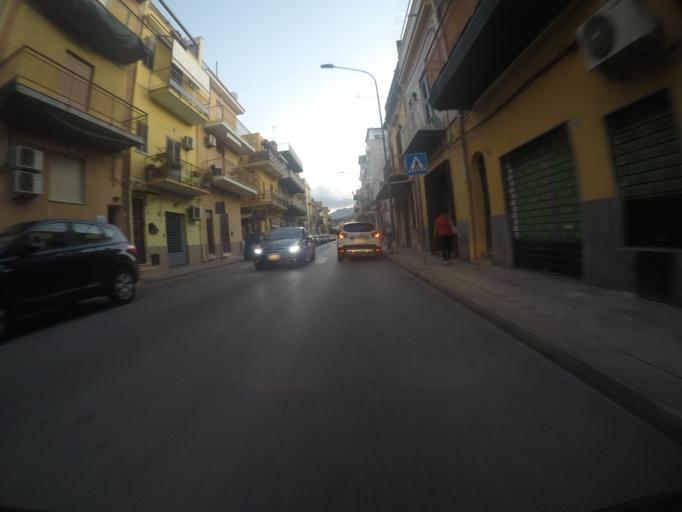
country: IT
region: Sicily
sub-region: Palermo
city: Capaci
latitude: 38.1743
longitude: 13.2412
